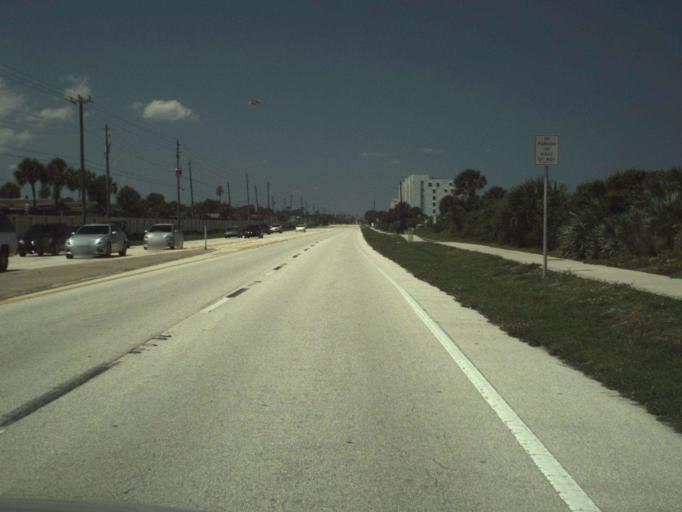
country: US
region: Florida
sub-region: Brevard County
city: South Patrick Shores
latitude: 28.1945
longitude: -80.5948
